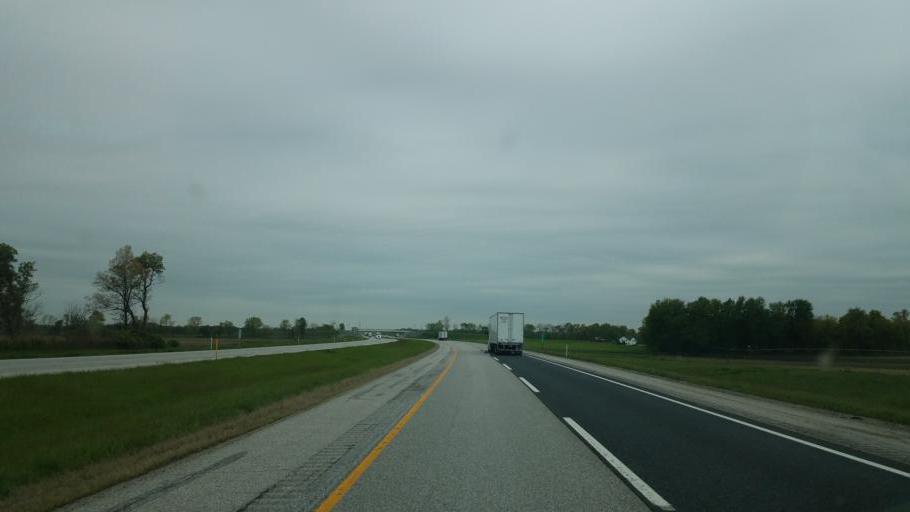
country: US
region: Michigan
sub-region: Saint Joseph County
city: Sturgis
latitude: 41.7533
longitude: -85.4774
